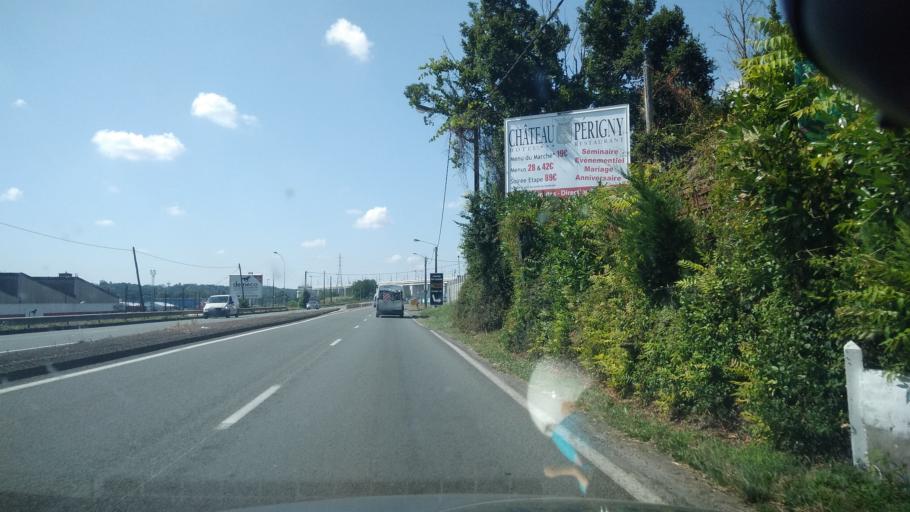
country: FR
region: Poitou-Charentes
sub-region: Departement de la Vienne
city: Chasseneuil-du-Poitou
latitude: 46.6269
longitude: 0.3547
